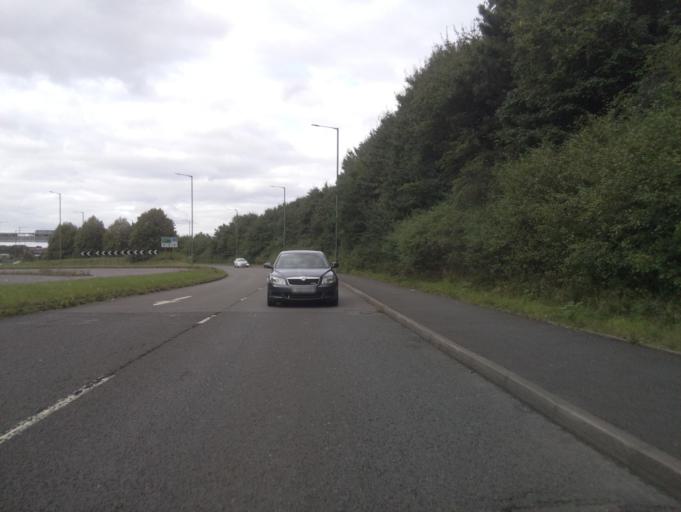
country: GB
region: England
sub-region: Solihull
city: Cheswick Green
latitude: 52.3782
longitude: -1.7848
